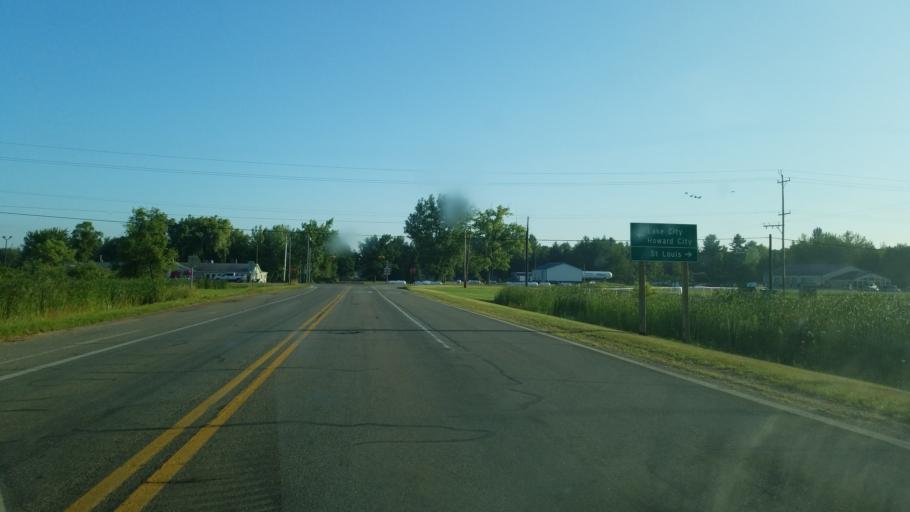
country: US
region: Michigan
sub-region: Montcalm County
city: Edmore
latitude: 43.4068
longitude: -85.0847
